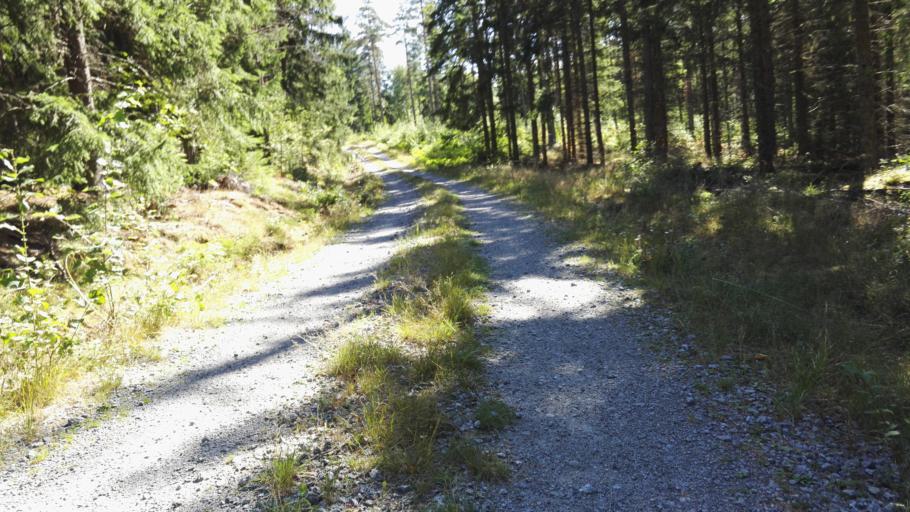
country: SE
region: Joenkoeping
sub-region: Vetlanda Kommun
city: Landsbro
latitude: 57.3226
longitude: 14.8600
